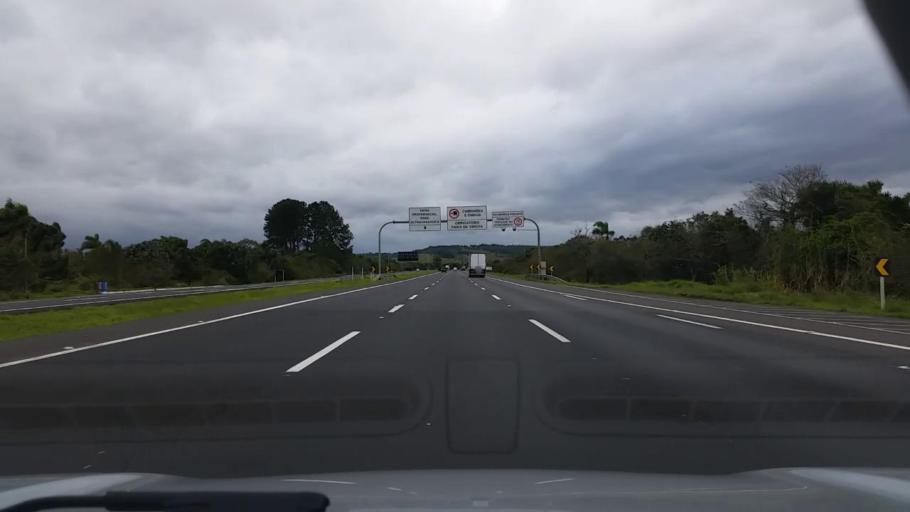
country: BR
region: Rio Grande do Sul
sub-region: Osorio
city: Osorio
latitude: -29.8872
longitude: -50.4539
